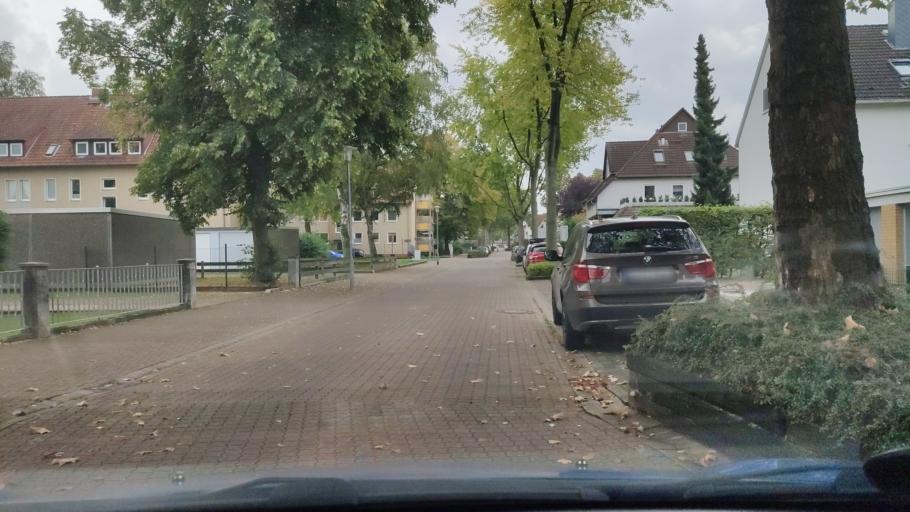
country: DE
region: Lower Saxony
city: Auf der Horst
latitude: 52.4022
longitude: 9.6421
